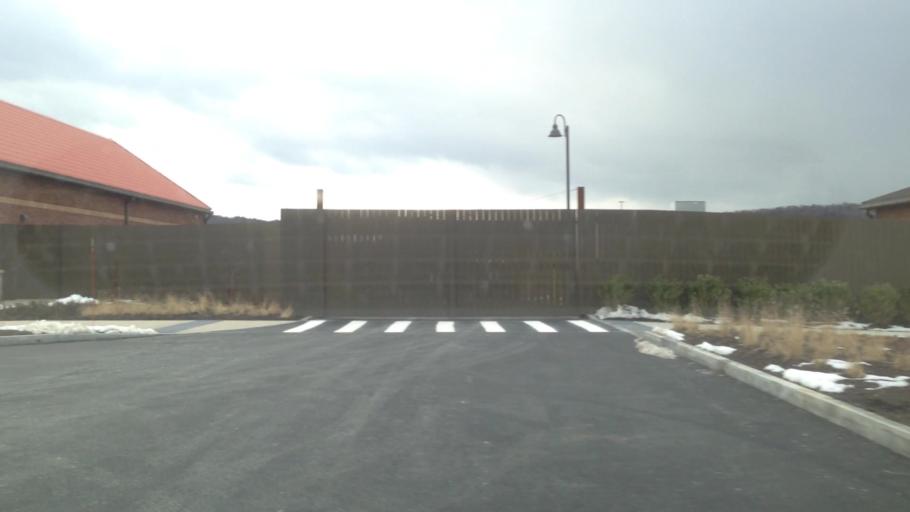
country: US
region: New York
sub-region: Albany County
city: Ravena
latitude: 42.4290
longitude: -73.8027
